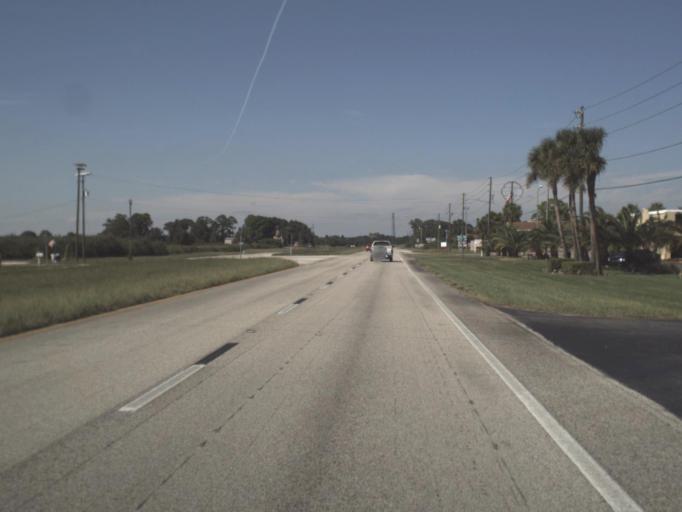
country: US
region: Florida
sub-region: Highlands County
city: Lake Placid
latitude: 27.2360
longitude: -81.3311
